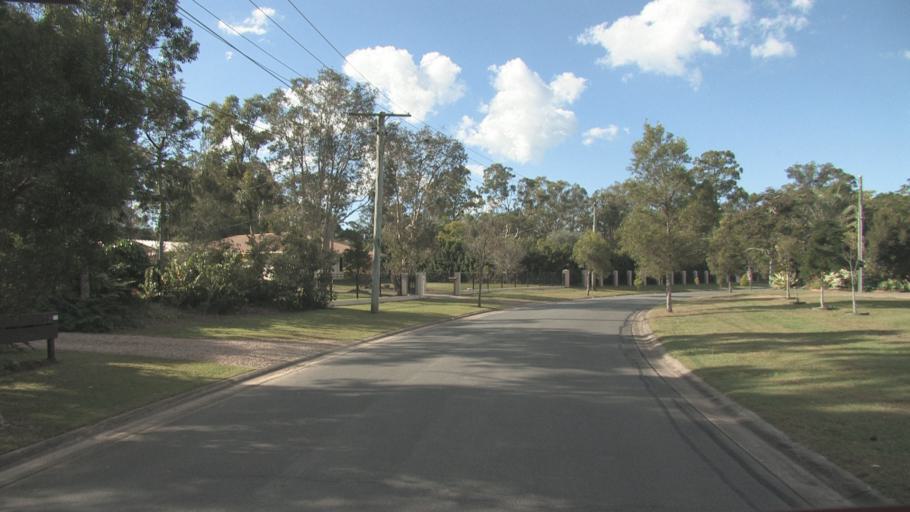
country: AU
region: Queensland
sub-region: Logan
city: Beenleigh
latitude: -27.6688
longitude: 153.2060
